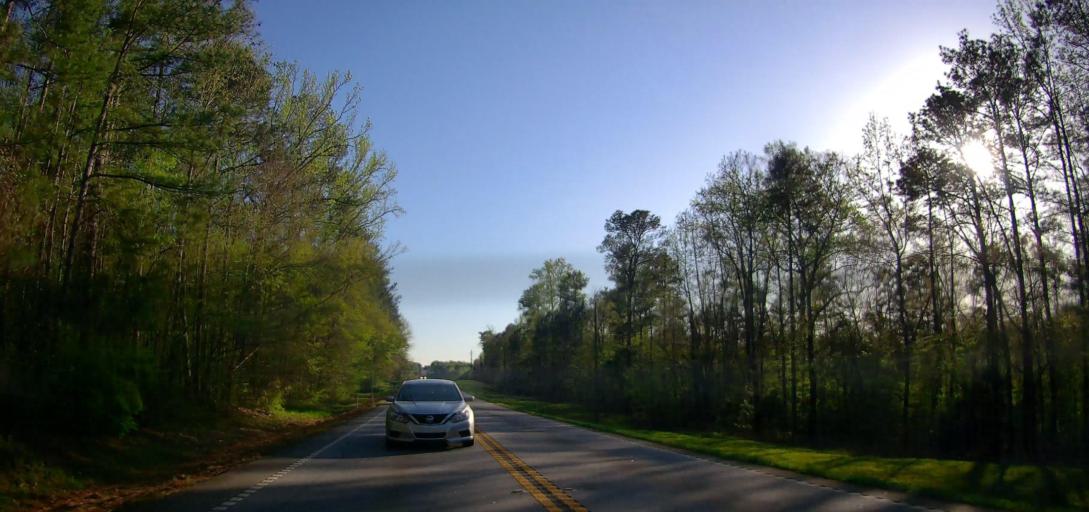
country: US
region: Georgia
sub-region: Butts County
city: Jackson
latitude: 33.4014
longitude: -83.8889
